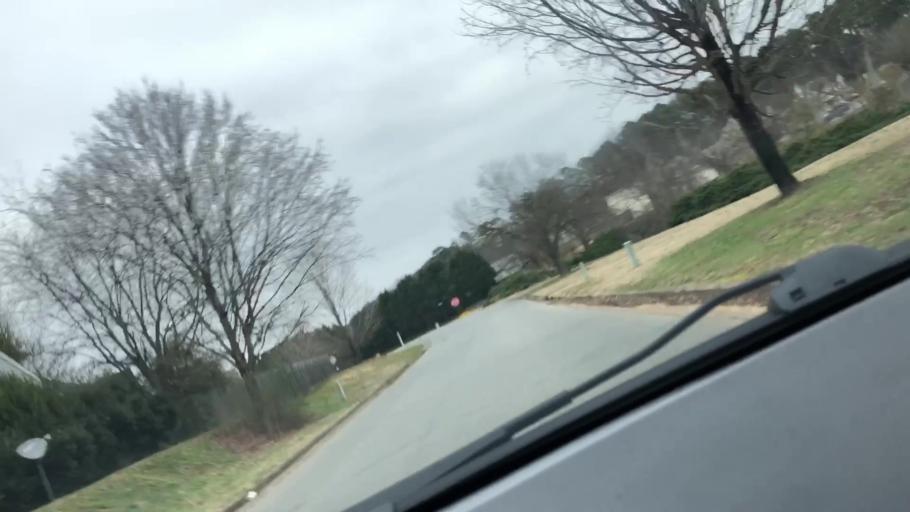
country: US
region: Georgia
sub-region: Bartow County
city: Cartersville
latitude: 34.2172
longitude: -84.8153
